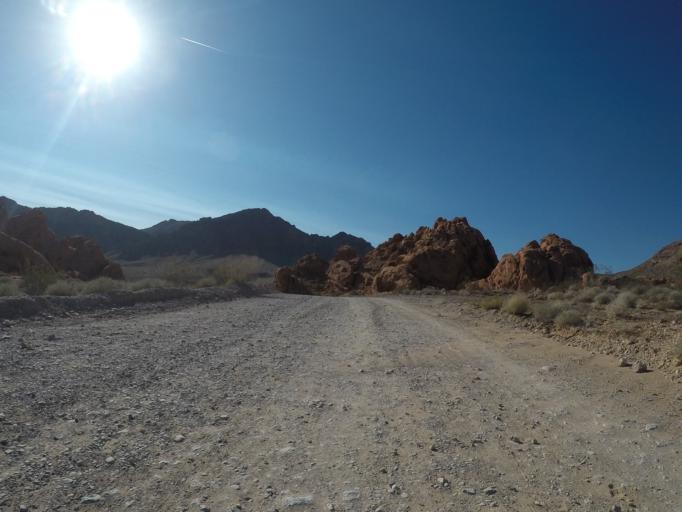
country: US
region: Nevada
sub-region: Clark County
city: Moapa Valley
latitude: 36.4133
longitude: -114.5587
